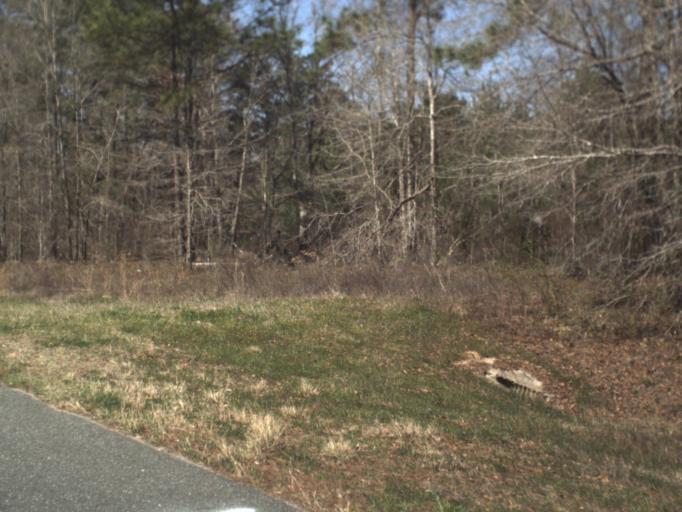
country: US
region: Florida
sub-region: Washington County
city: Chipley
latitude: 30.7895
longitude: -85.4126
